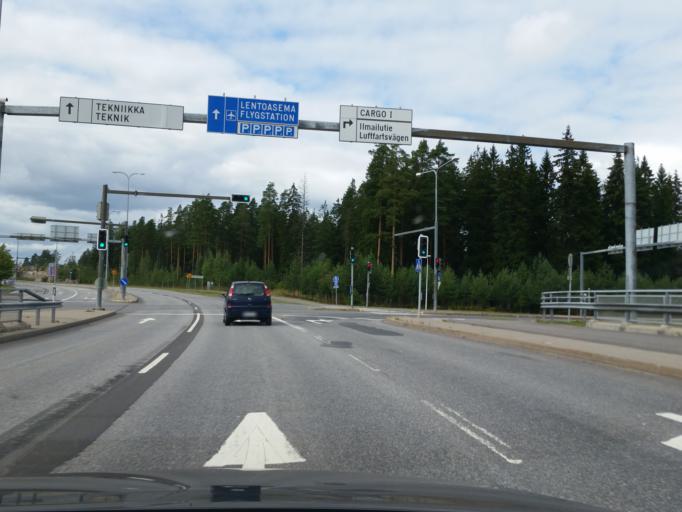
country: FI
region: Uusimaa
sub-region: Helsinki
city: Vantaa
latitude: 60.3054
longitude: 24.9757
